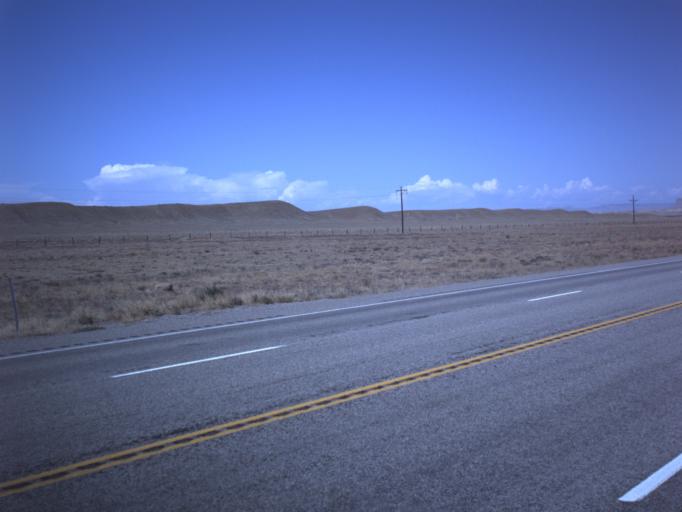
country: US
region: Utah
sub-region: Grand County
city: Moab
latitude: 38.8261
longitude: -109.7825
